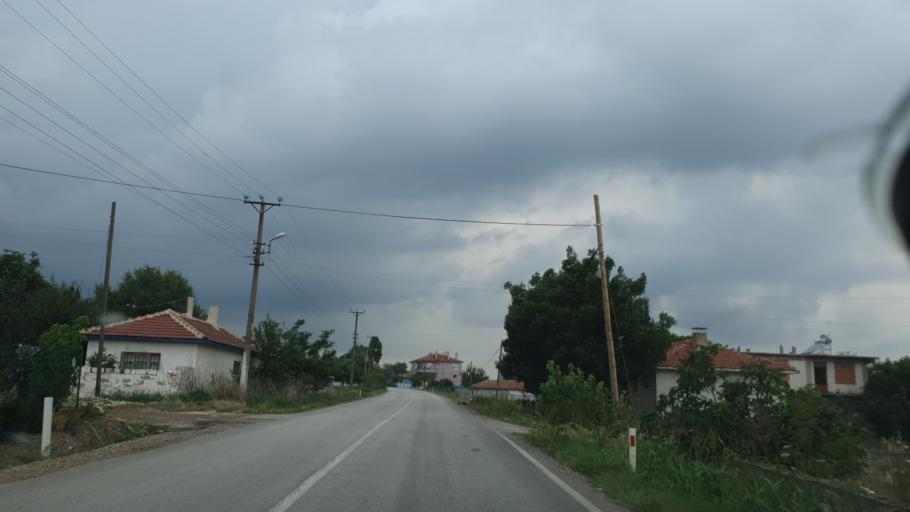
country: TR
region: Tekirdag
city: Hayrabolu
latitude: 41.2200
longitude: 26.9861
